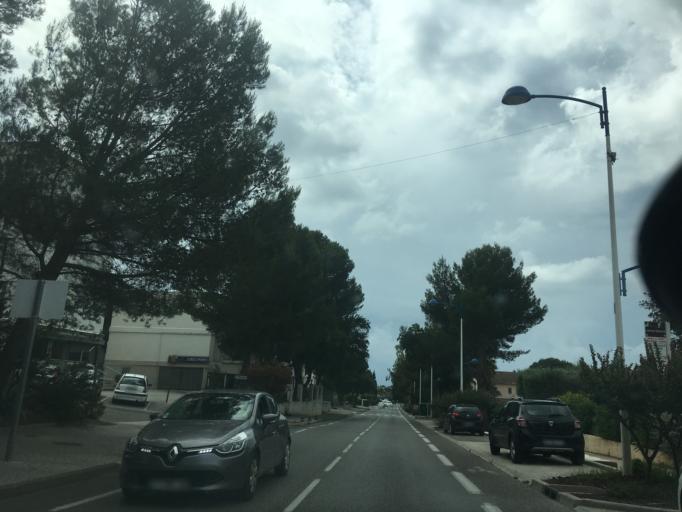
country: FR
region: Provence-Alpes-Cote d'Azur
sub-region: Departement du Var
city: La Londe-les-Maures
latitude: 43.1318
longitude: 6.2389
